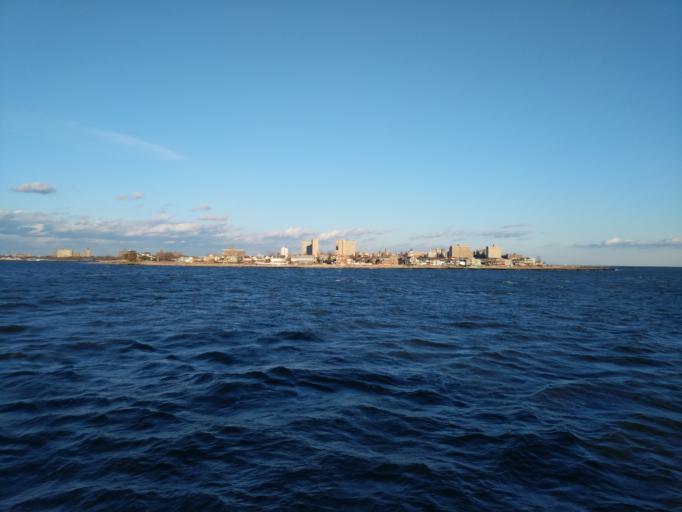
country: US
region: New York
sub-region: Kings County
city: Coney Island
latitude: 40.5772
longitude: -74.0191
